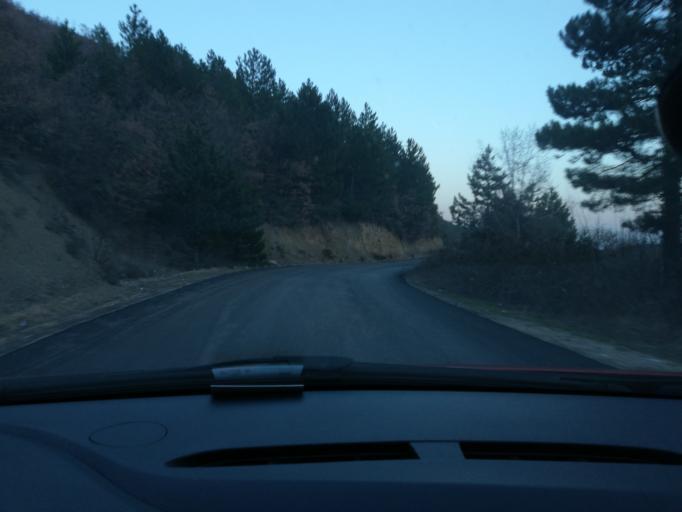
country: TR
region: Karabuk
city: Karabuk
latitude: 41.2719
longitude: 32.6279
